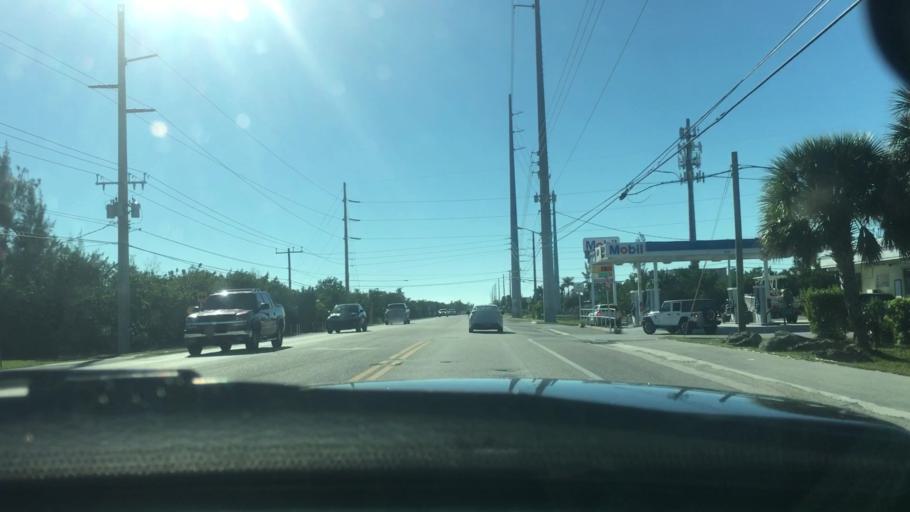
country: US
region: Florida
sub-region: Monroe County
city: Big Coppitt Key
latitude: 24.5964
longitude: -81.6583
